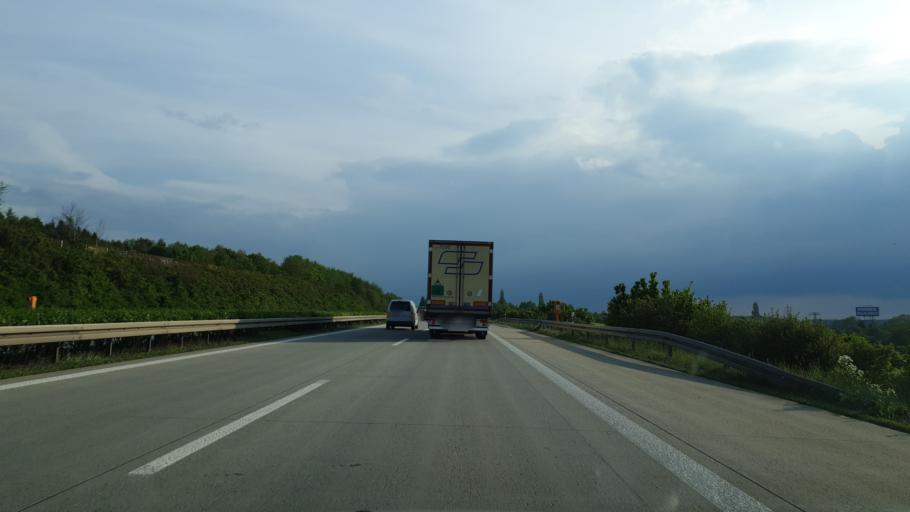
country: DE
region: Saxony
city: Stollberg
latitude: 50.7177
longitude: 12.7642
